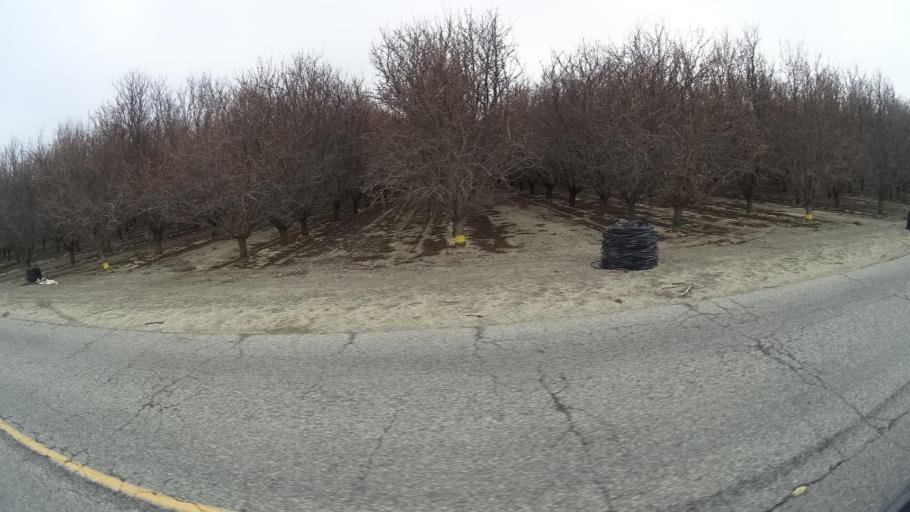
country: US
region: California
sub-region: Kern County
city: Maricopa
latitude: 35.1231
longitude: -119.3559
